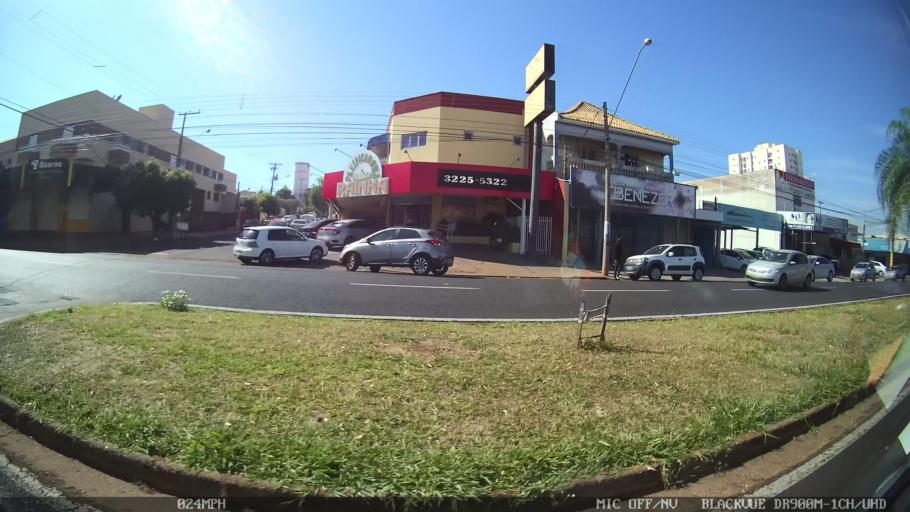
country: BR
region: Sao Paulo
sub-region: Sao Jose Do Rio Preto
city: Sao Jose do Rio Preto
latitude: -20.7846
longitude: -49.3686
